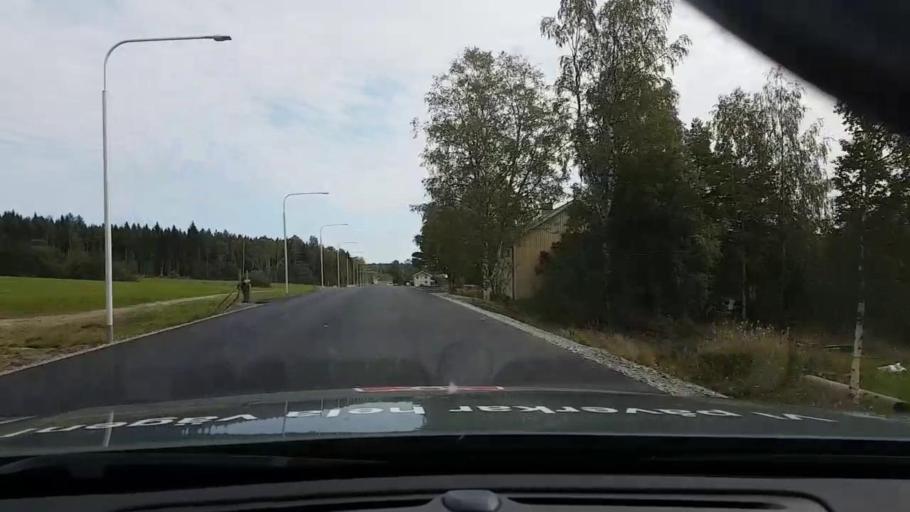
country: SE
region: Vaesternorrland
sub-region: OErnskoeldsviks Kommun
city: Bjasta
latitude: 63.2932
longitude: 18.4764
